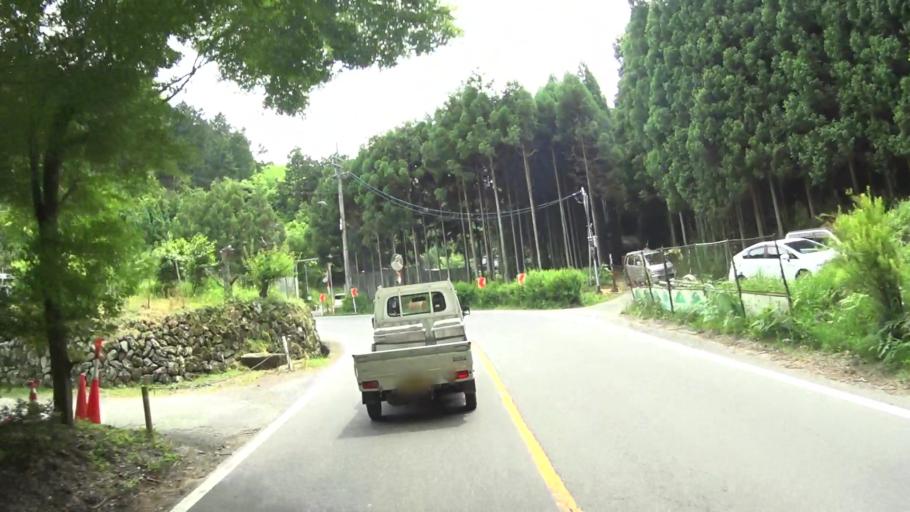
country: JP
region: Kyoto
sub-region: Kyoto-shi
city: Kamigyo-ku
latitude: 35.0526
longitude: 135.6784
